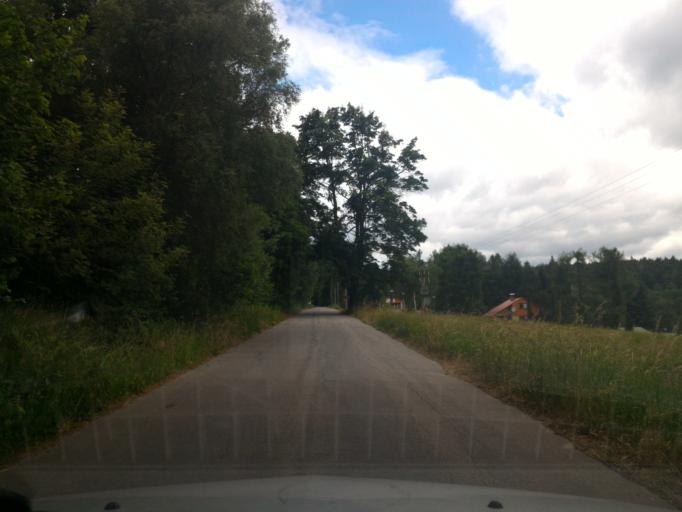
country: CZ
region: Vysocina
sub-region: Okres Jihlava
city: Telc
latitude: 49.2272
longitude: 15.3849
